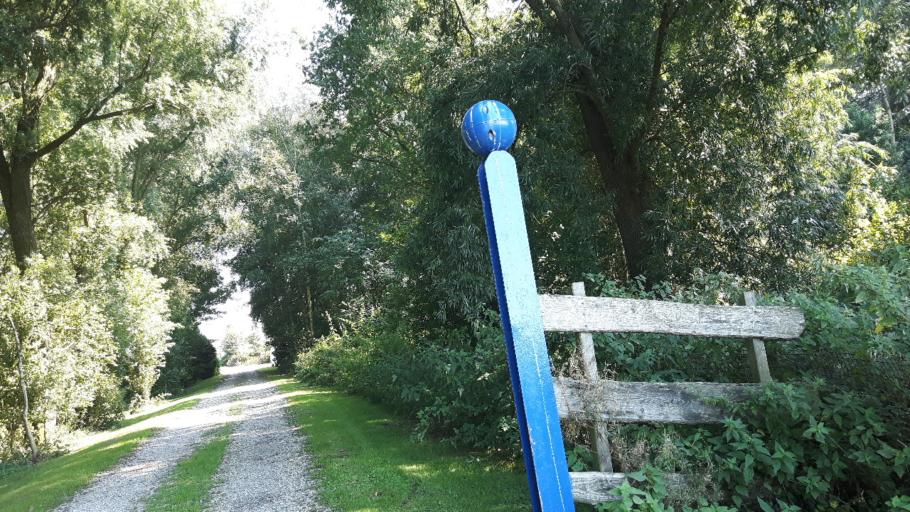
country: NL
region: Drenthe
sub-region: Gemeente Tynaarlo
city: Zuidlaren
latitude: 53.1454
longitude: 6.6865
